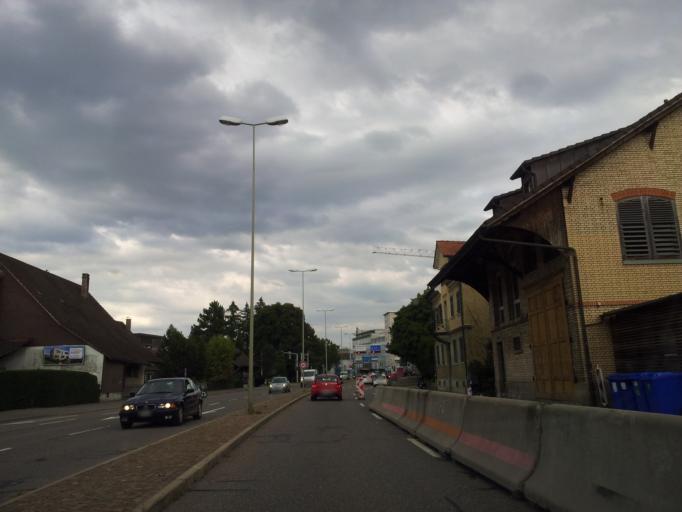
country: CH
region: Zurich
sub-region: Bezirk Dietikon
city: Schlieren / Freiestrasse
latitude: 47.3974
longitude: 8.4445
